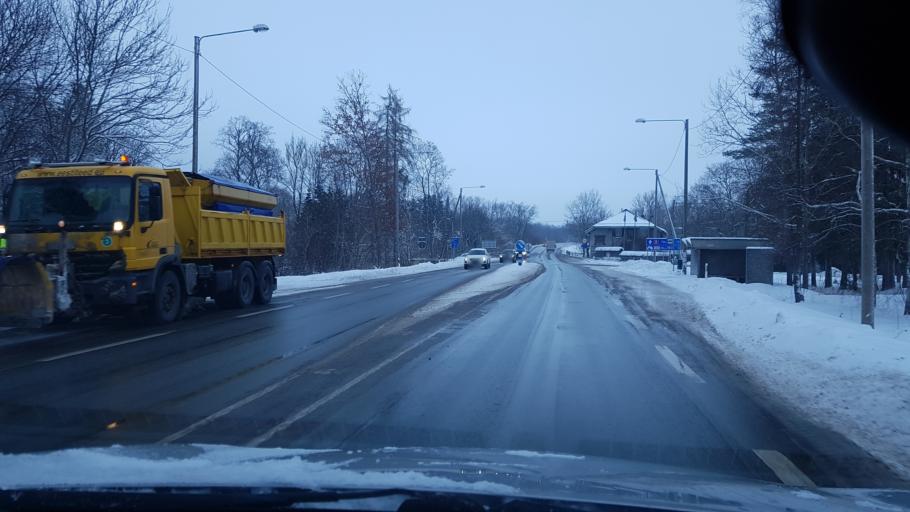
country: EE
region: Harju
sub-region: Harku vald
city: Tabasalu
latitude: 59.3784
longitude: 24.5380
